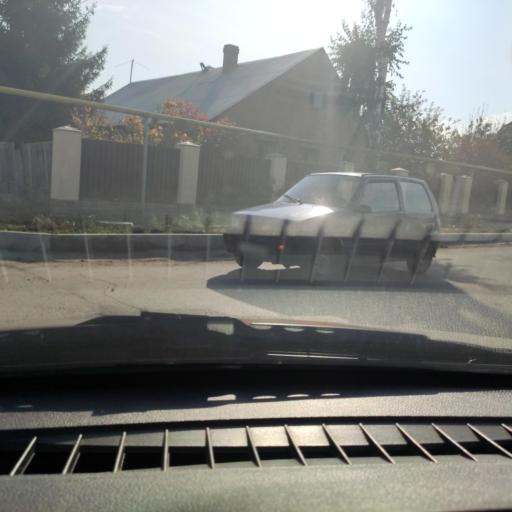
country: RU
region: Samara
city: Podstepki
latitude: 53.5131
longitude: 49.2371
